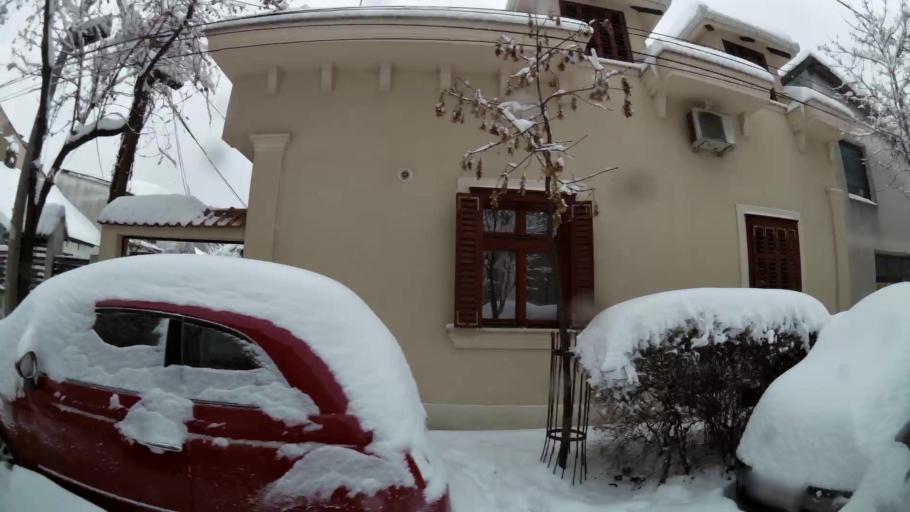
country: RS
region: Central Serbia
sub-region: Belgrade
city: Vracar
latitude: 44.7903
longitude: 20.4810
